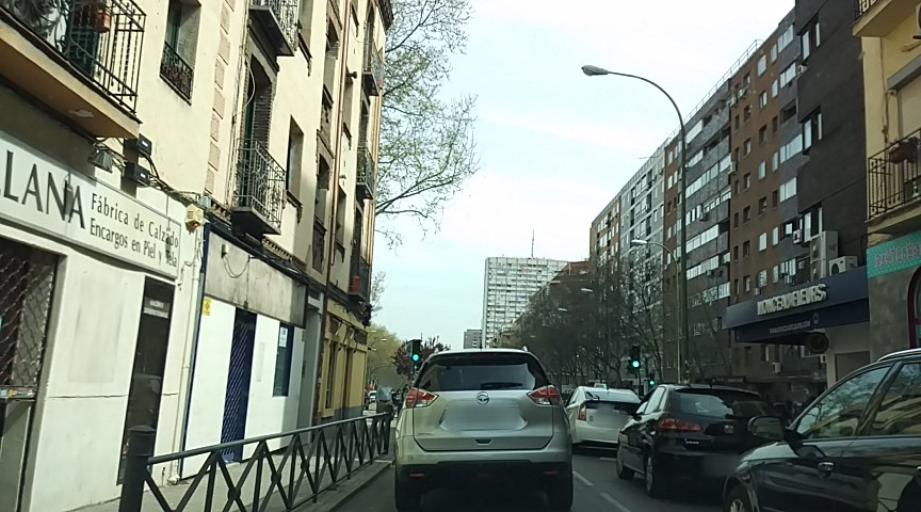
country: ES
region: Madrid
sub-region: Provincia de Madrid
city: Chamberi
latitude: 40.4526
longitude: -3.6999
